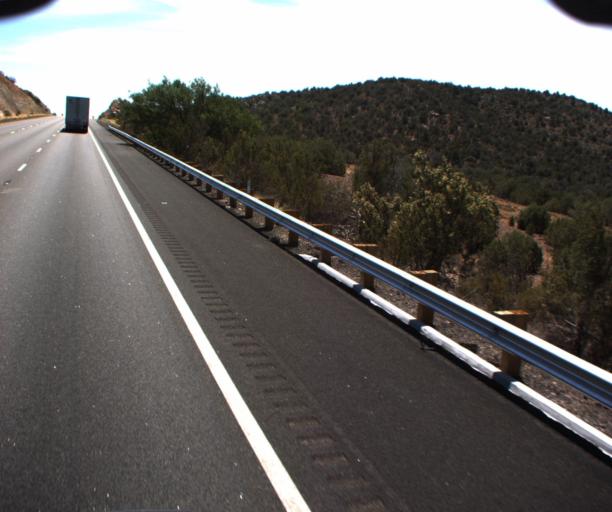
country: US
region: Arizona
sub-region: Mohave County
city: Peach Springs
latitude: 35.1863
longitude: -113.4100
